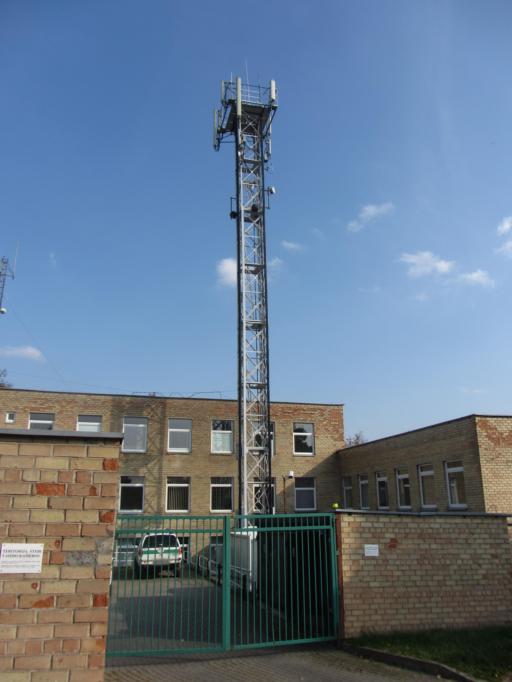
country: LT
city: Trakai
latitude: 54.6397
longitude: 24.9323
